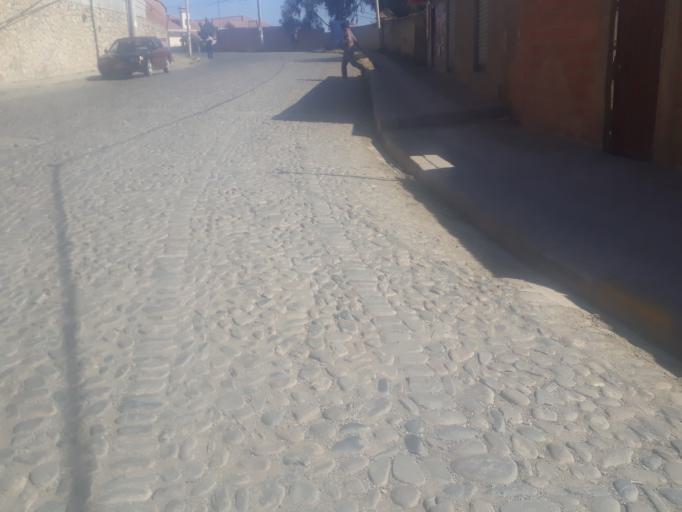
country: BO
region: La Paz
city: La Paz
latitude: -16.5384
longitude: -68.0570
